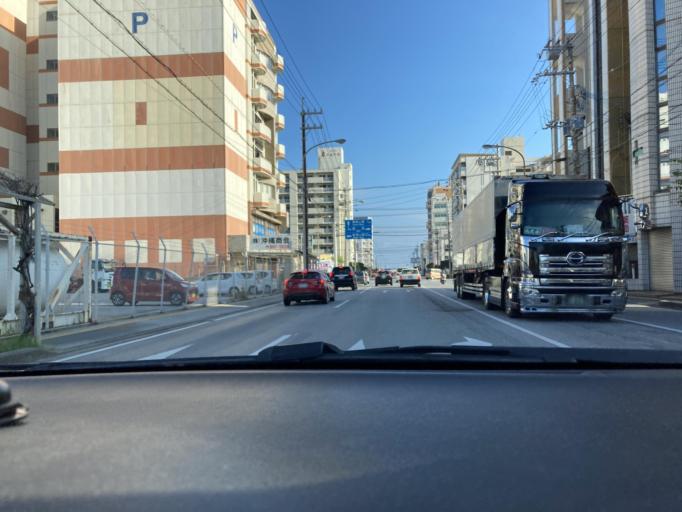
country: JP
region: Okinawa
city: Naha-shi
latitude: 26.2404
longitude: 127.6816
